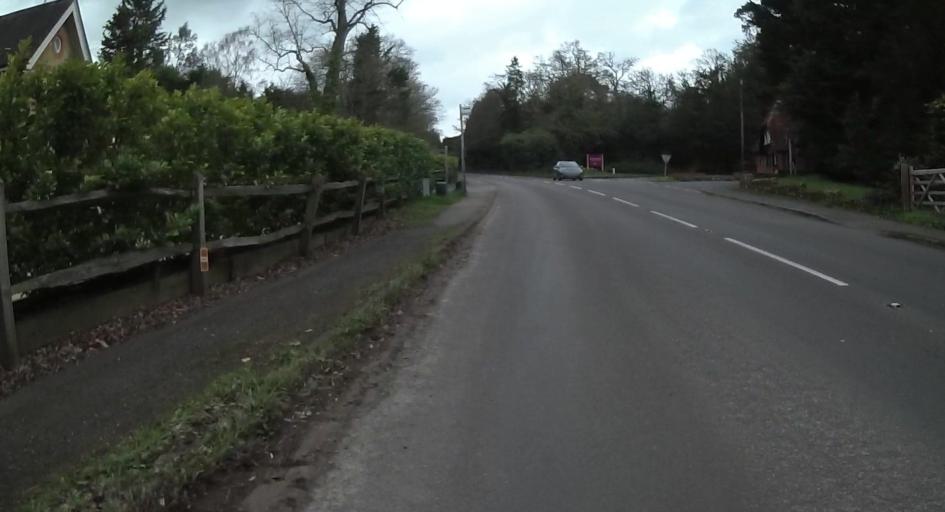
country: GB
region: England
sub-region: Surrey
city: Churt
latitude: 51.1714
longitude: -0.7870
